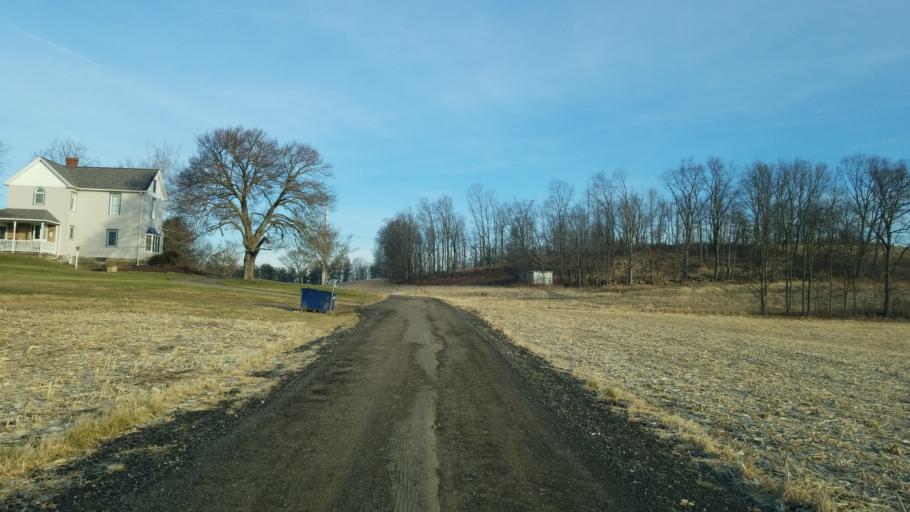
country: US
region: Pennsylvania
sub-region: Indiana County
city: Chevy Chase Heights
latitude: 40.8481
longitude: -79.2620
